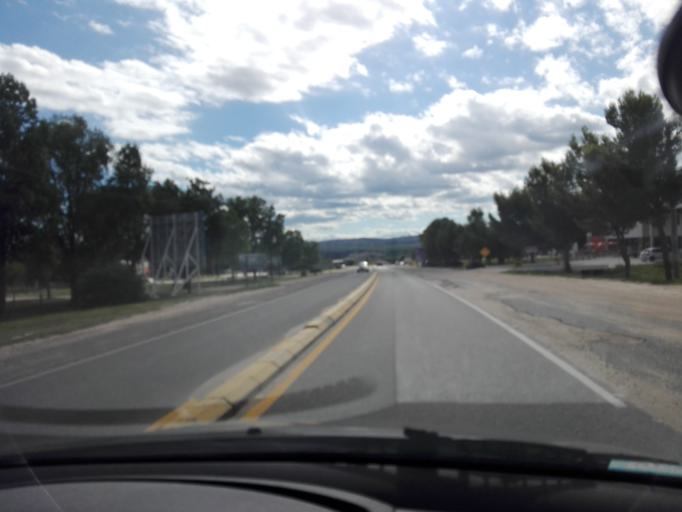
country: AR
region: Cordoba
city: Mina Clavero
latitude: -31.7418
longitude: -65.0022
